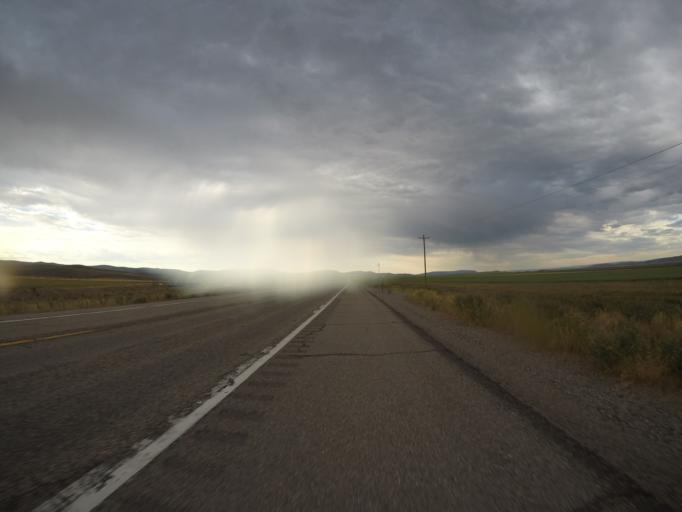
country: US
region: Utah
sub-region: Rich County
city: Randolph
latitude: 41.9302
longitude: -110.9549
